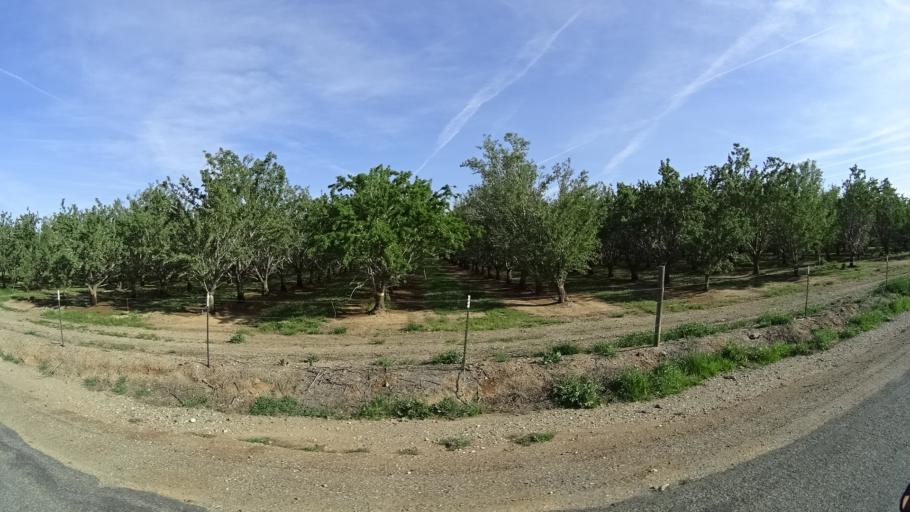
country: US
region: California
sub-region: Glenn County
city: Orland
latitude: 39.6687
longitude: -122.2902
